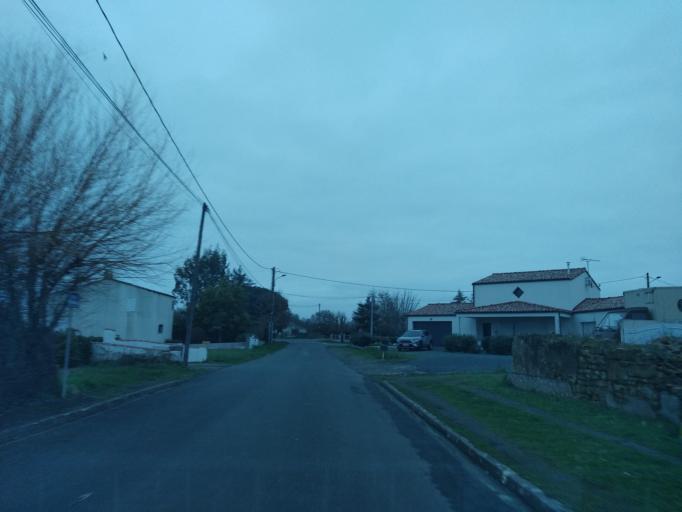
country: FR
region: Pays de la Loire
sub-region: Departement de la Vendee
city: Triaize
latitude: 46.4112
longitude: -1.2611
